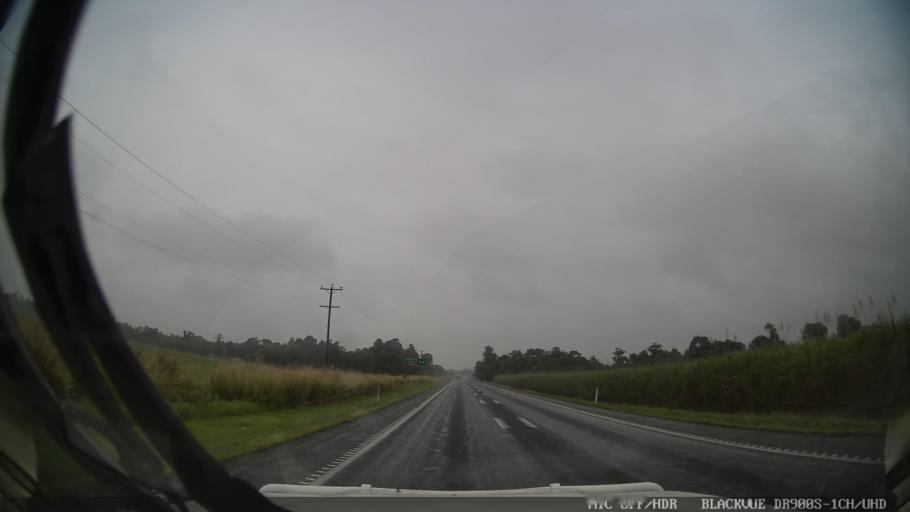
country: AU
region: Queensland
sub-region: Cassowary Coast
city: Innisfail
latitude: -17.7561
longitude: 146.0279
